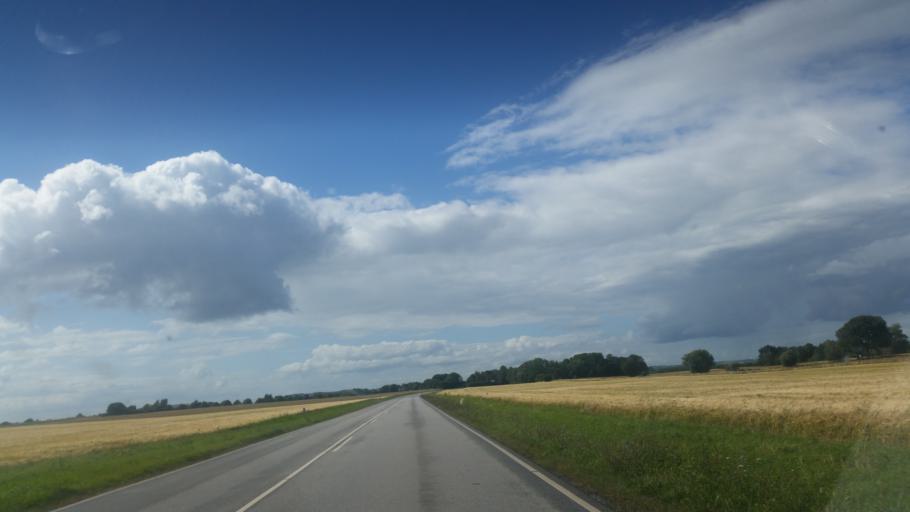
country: DK
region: Zealand
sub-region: Holbaek Kommune
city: Svinninge
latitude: 55.7385
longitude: 11.5439
